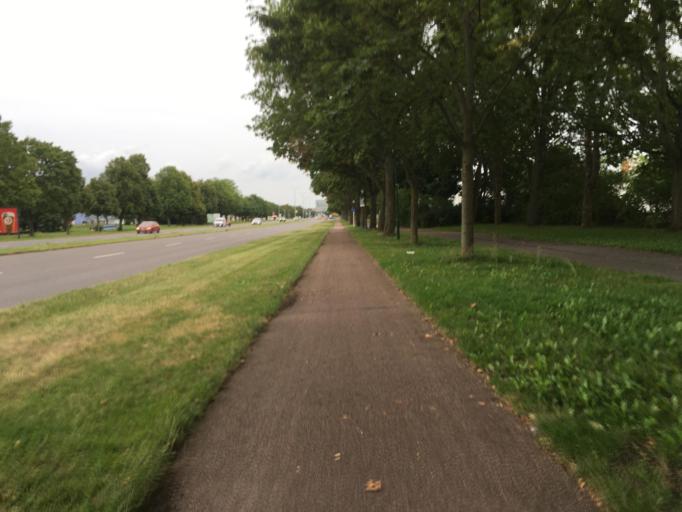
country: DE
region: Brandenburg
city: Schwedt (Oder)
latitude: 53.0662
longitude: 14.2645
